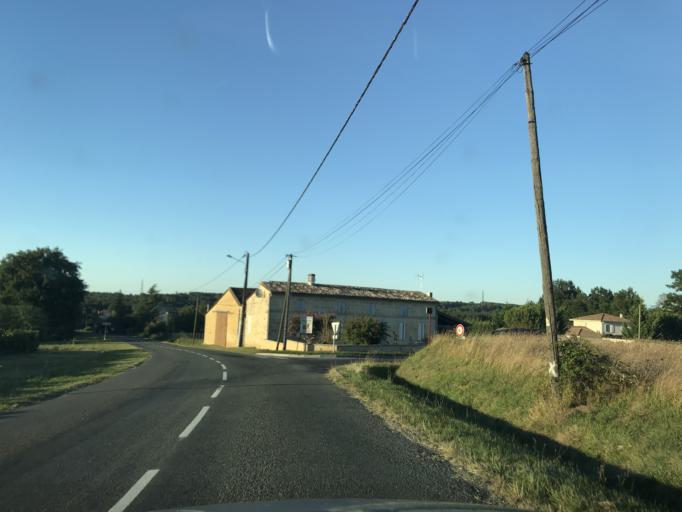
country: FR
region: Aquitaine
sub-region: Departement de la Gironde
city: Saint-Medard-de-Guizieres
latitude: 44.9775
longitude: -0.0639
